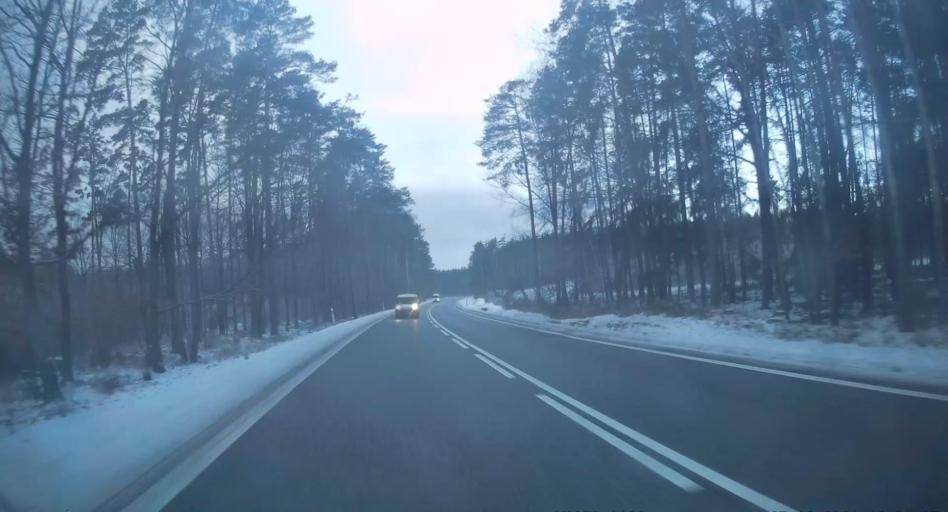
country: PL
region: Swietokrzyskie
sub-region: Powiat konecki
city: Radoszyce
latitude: 51.0985
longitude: 20.3262
